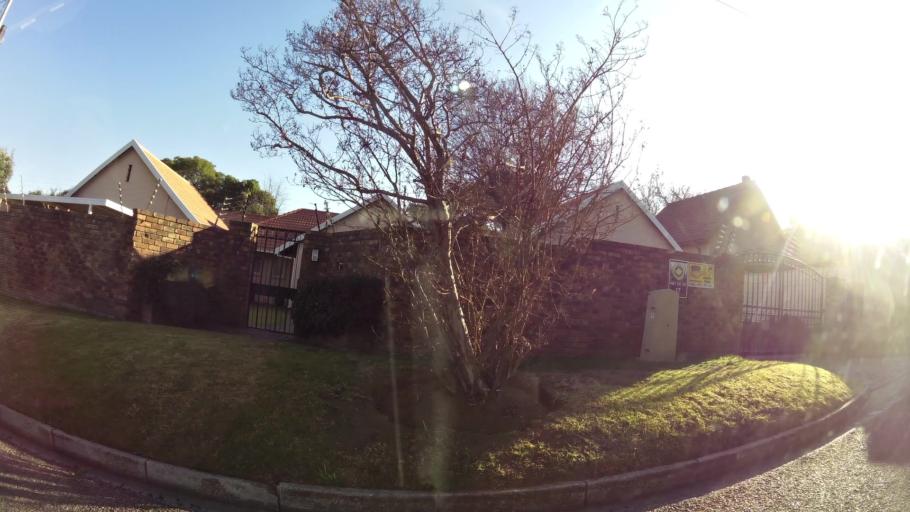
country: ZA
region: Gauteng
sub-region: City of Johannesburg Metropolitan Municipality
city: Johannesburg
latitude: -26.1287
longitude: 28.0773
